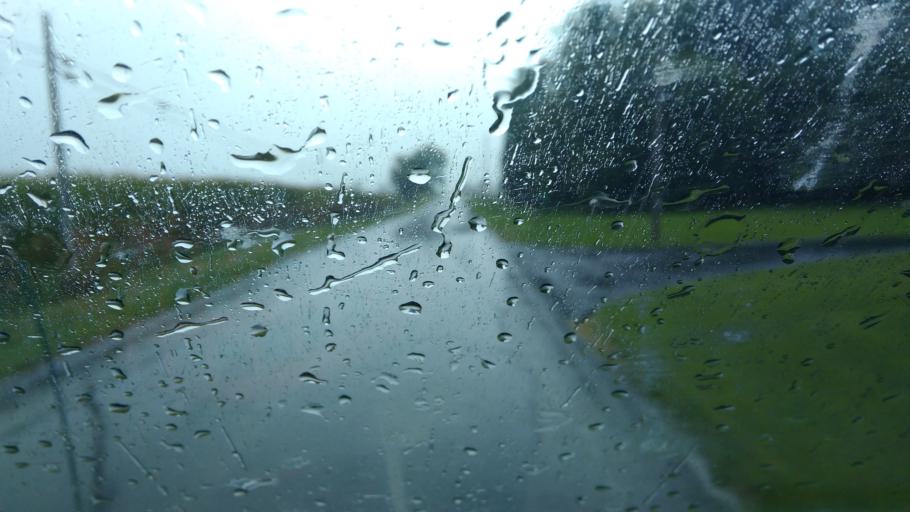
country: US
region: Ohio
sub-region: Hardin County
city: Kenton
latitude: 40.6822
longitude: -83.5379
